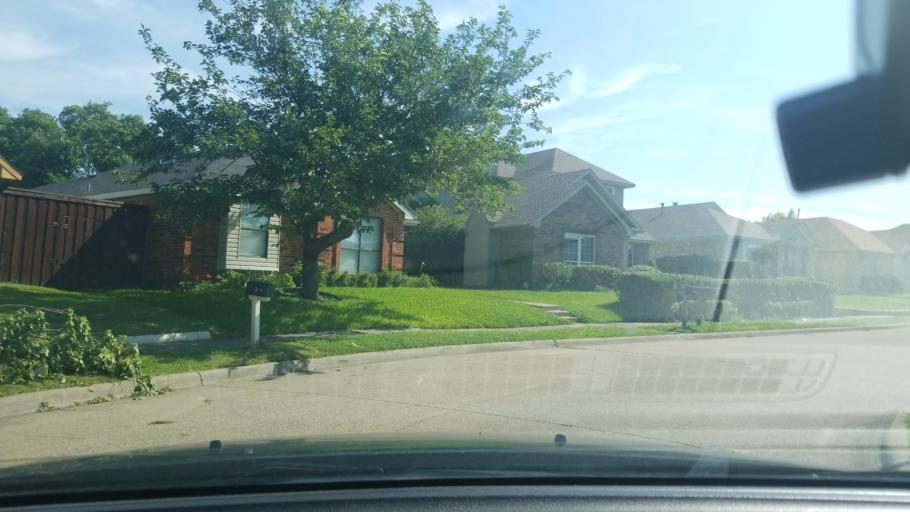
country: US
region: Texas
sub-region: Dallas County
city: Mesquite
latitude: 32.7773
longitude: -96.5959
